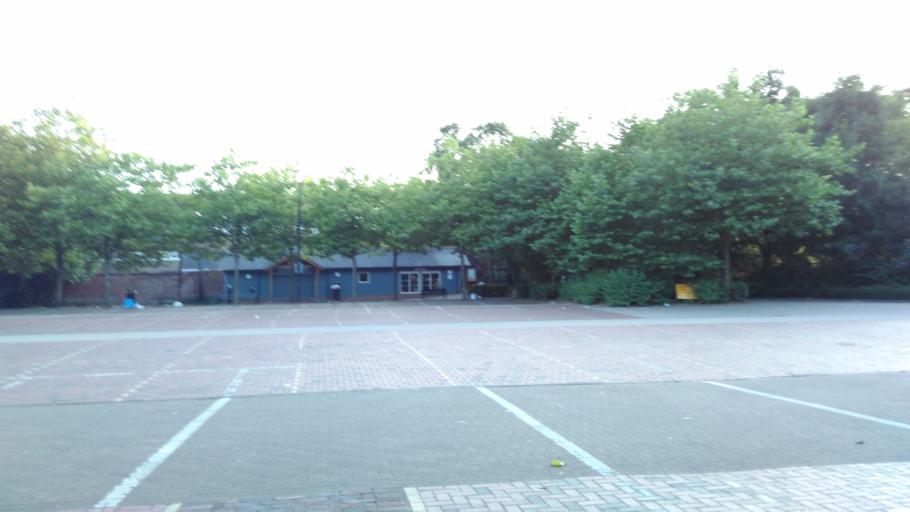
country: GB
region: England
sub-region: Kent
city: Canterbury
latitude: 51.2845
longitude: 1.0838
